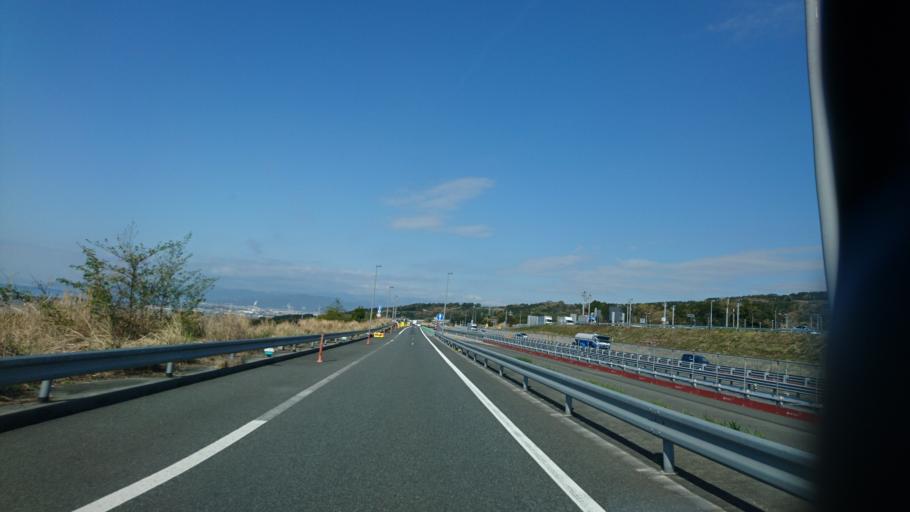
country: JP
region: Shizuoka
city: Numazu
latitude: 35.1531
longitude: 138.8078
